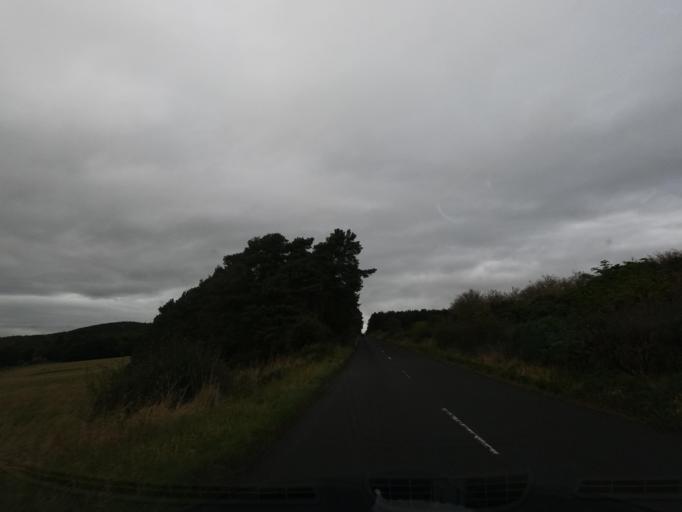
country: GB
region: England
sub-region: Northumberland
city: Doddington
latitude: 55.5991
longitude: -2.0024
